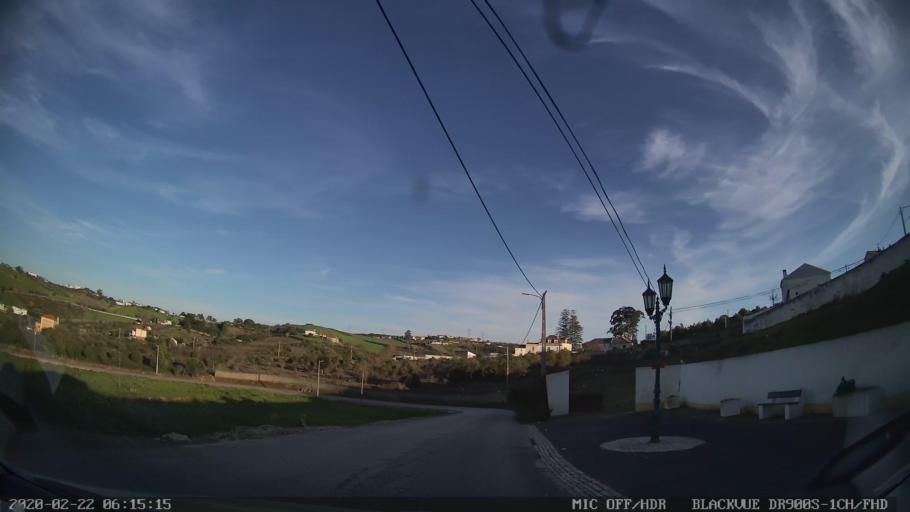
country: PT
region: Lisbon
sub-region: Vila Franca de Xira
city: Vila Franca de Xira
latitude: 38.9859
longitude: -9.0152
